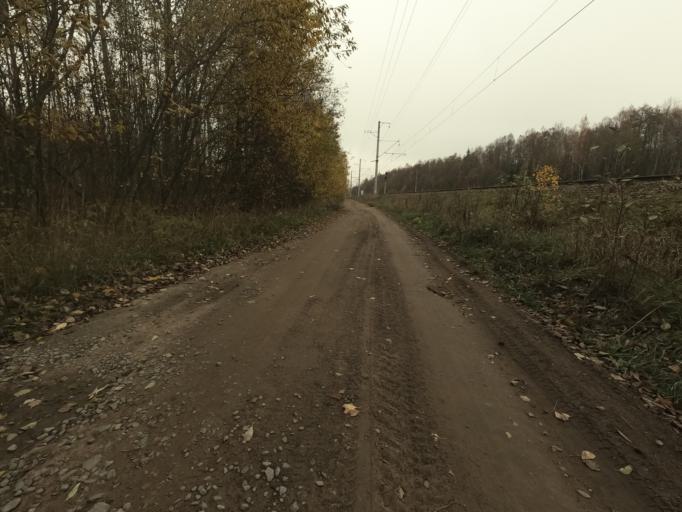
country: RU
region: Leningrad
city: Pavlovo
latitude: 59.7860
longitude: 30.8911
